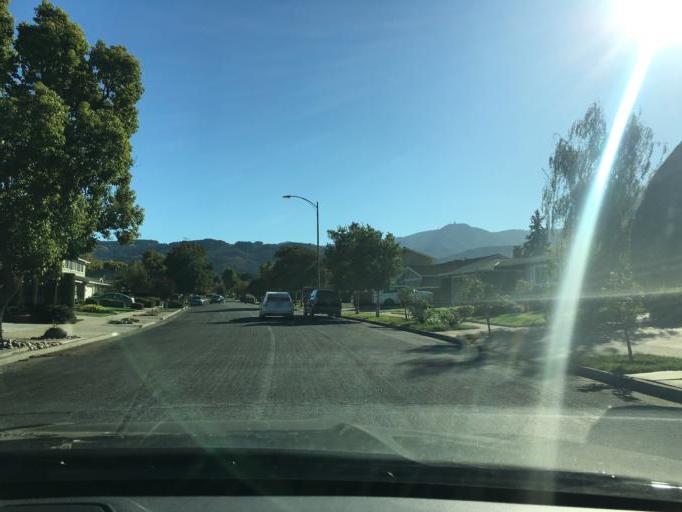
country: US
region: California
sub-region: Santa Clara County
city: Seven Trees
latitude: 37.2202
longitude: -121.8552
